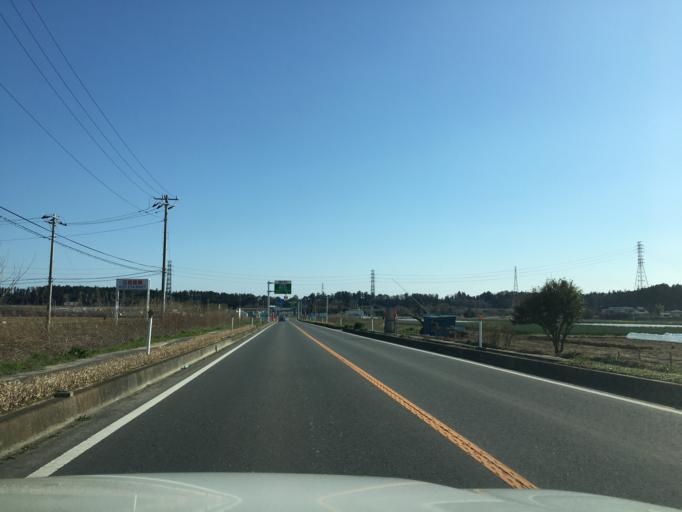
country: JP
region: Ibaraki
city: Mito-shi
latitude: 36.4220
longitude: 140.4229
